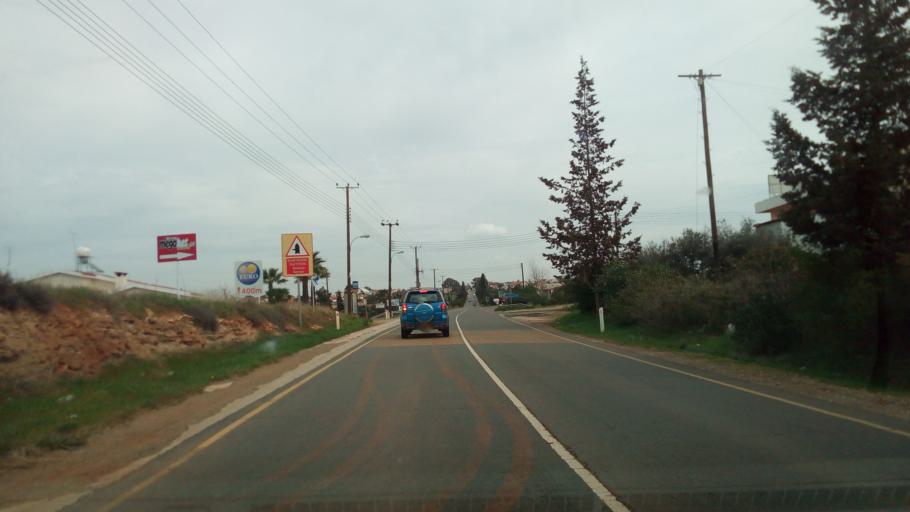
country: CY
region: Lefkosia
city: Astromeritis
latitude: 35.1369
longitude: 33.0274
